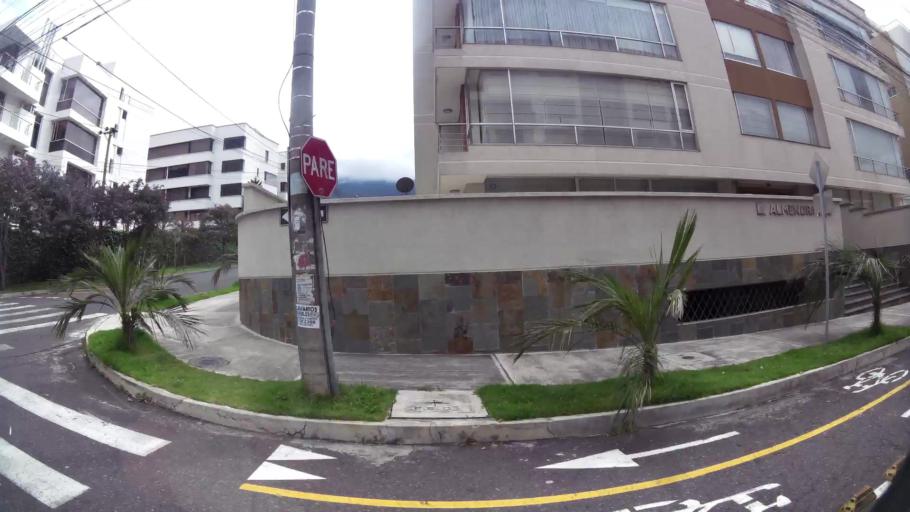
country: EC
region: Pichincha
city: Quito
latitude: -0.1673
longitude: -78.4880
